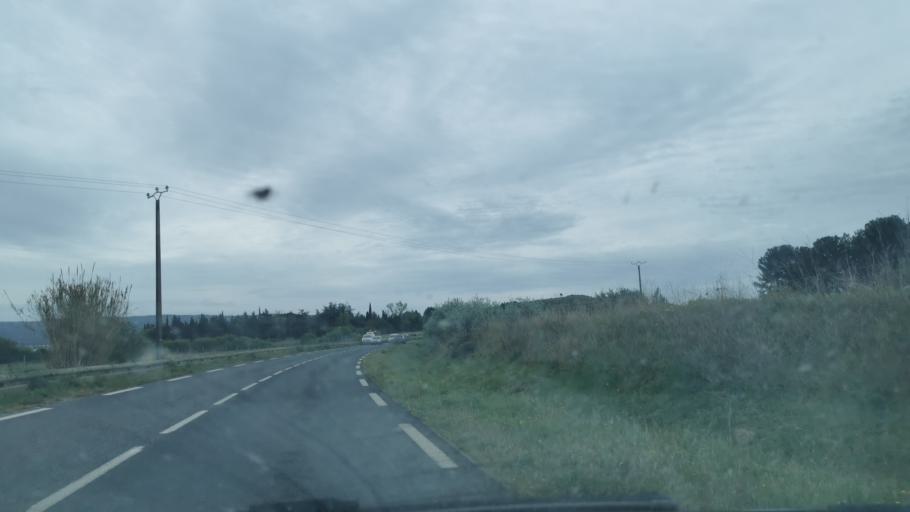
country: FR
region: Languedoc-Roussillon
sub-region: Departement de l'Herault
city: Montbazin
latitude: 43.5119
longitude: 3.6826
